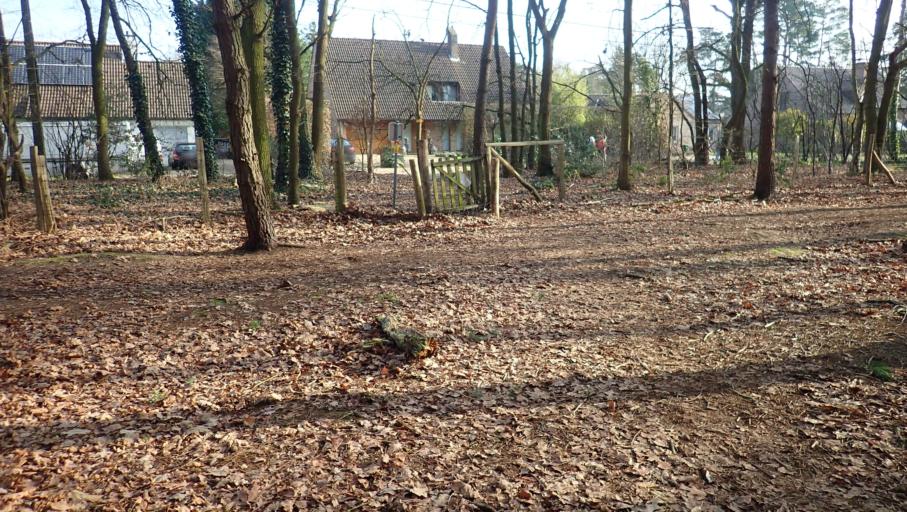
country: BE
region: Flanders
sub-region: Provincie Vlaams-Brabant
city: Tremelo
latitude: 51.0121
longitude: 4.7204
